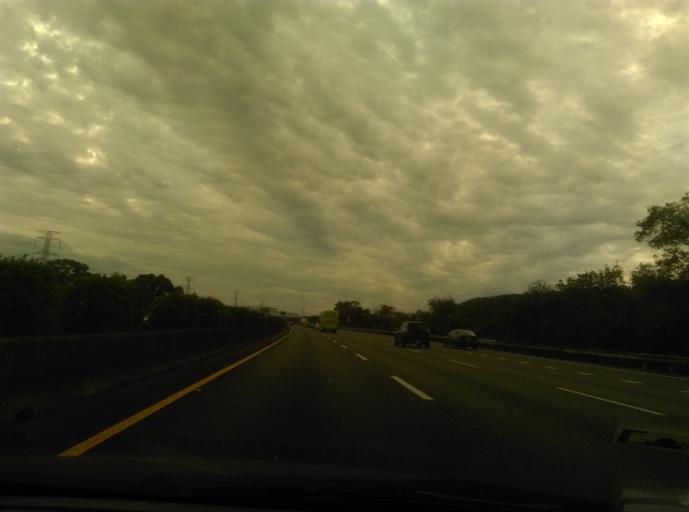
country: TW
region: Taiwan
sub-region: Taoyuan
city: Taoyuan
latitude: 24.9350
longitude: 121.3167
